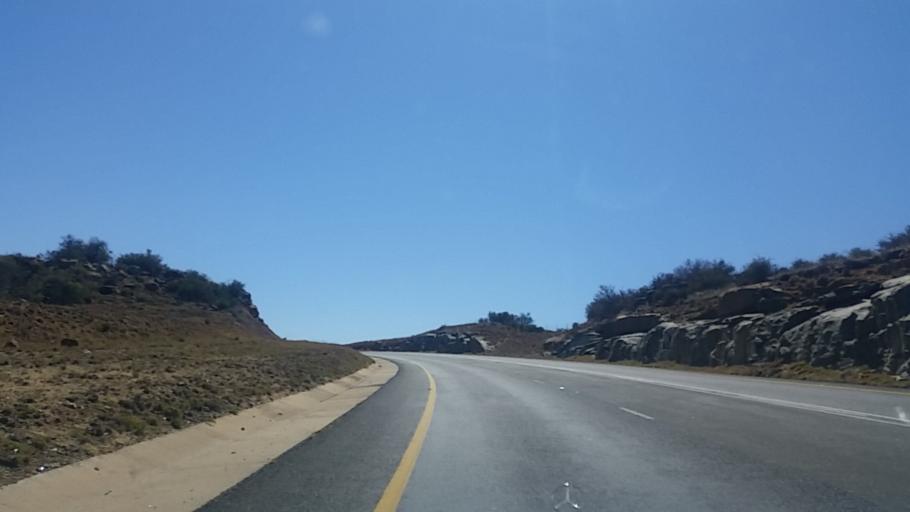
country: ZA
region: Eastern Cape
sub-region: Cacadu District Municipality
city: Graaff-Reinet
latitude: -32.0572
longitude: 24.6114
